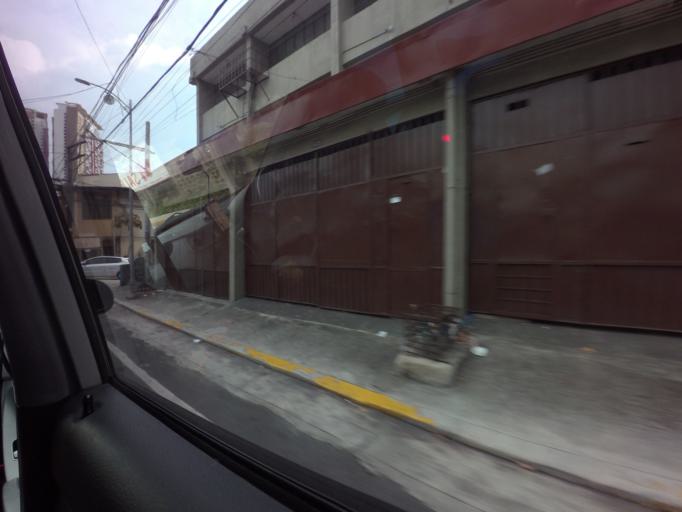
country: PH
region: Metro Manila
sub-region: San Juan
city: San Juan
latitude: 14.6060
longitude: 121.0140
